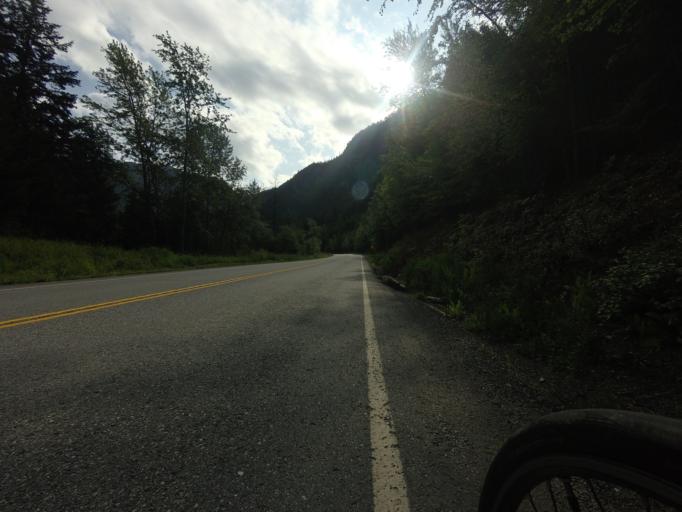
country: CA
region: British Columbia
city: Lillooet
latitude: 50.6377
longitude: -122.0795
